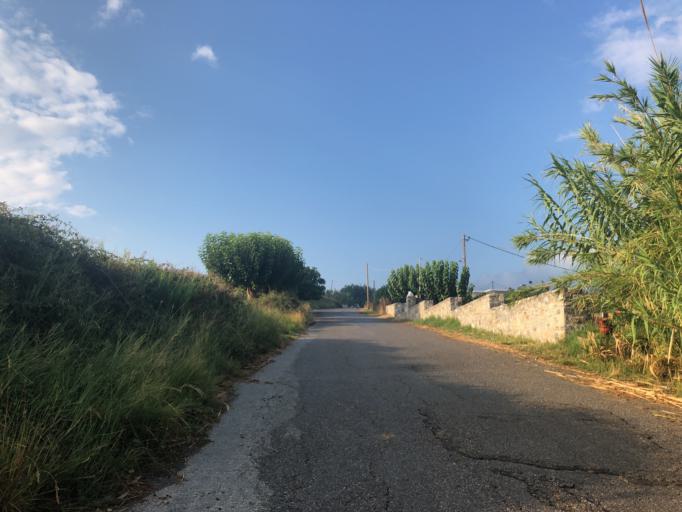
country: GR
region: Crete
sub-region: Nomos Chanias
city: Georgioupolis
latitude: 35.3492
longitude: 24.3148
